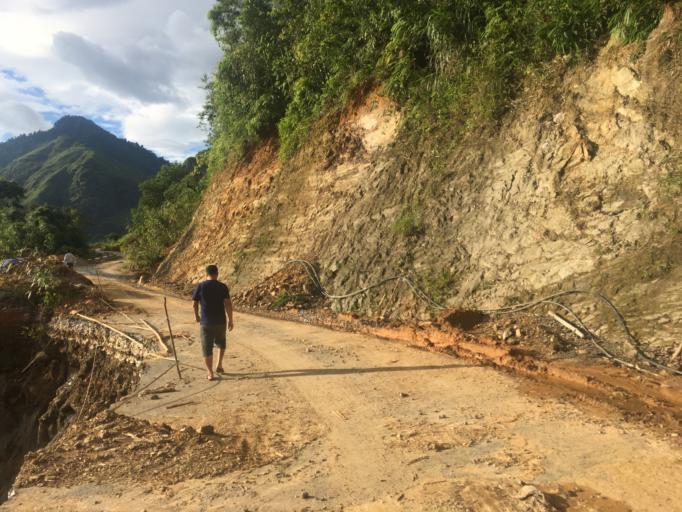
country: VN
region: Ha Giang
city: Thi Tran Tam Son
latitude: 22.9477
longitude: 105.0259
